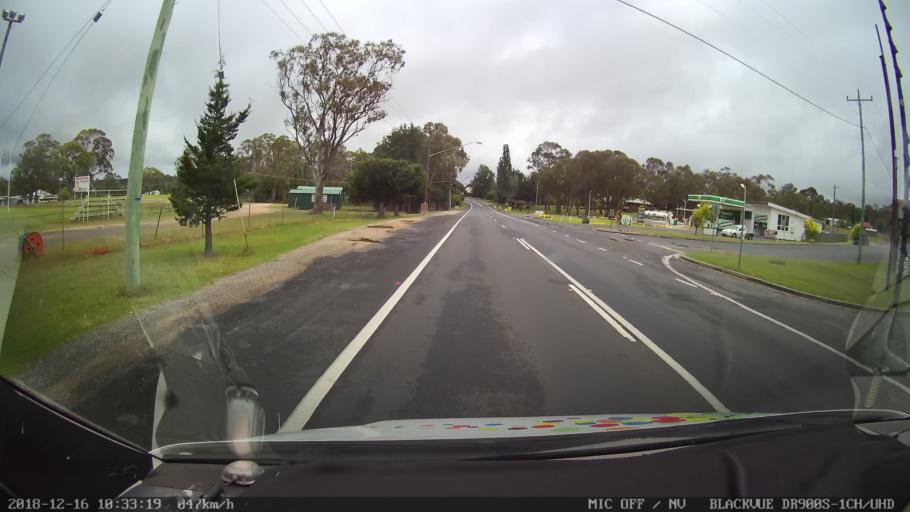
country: AU
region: New South Wales
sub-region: Tenterfield Municipality
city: Carrolls Creek
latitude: -29.0655
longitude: 152.0159
